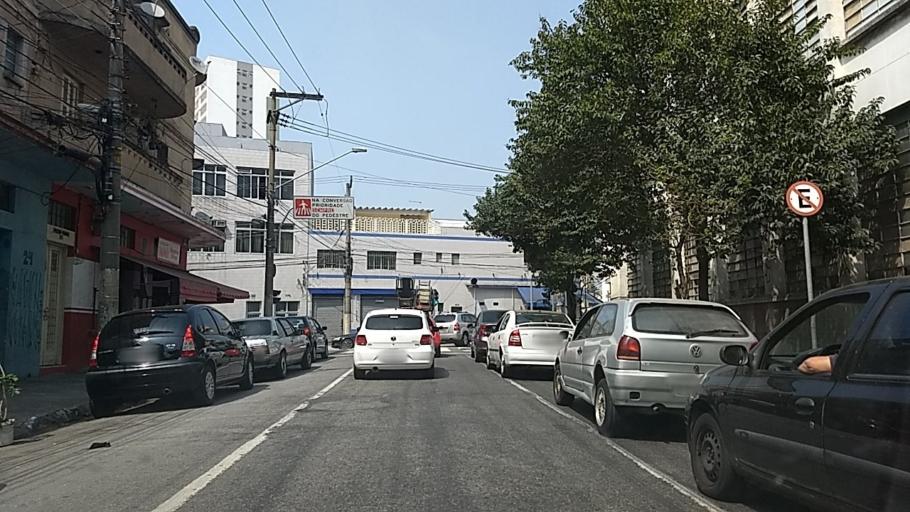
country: BR
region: Sao Paulo
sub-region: Sao Paulo
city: Sao Paulo
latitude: -23.5360
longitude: -46.6049
